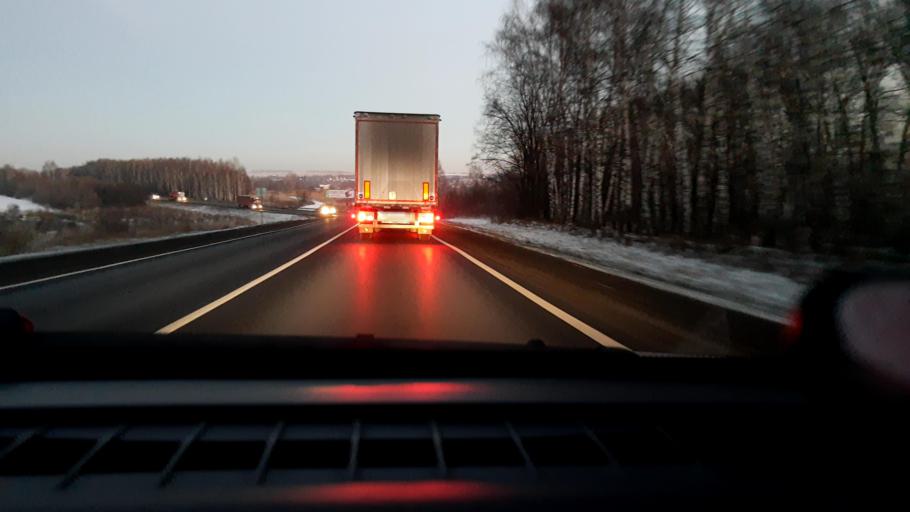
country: RU
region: Nizjnij Novgorod
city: Lyskovo
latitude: 56.0060
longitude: 44.8884
